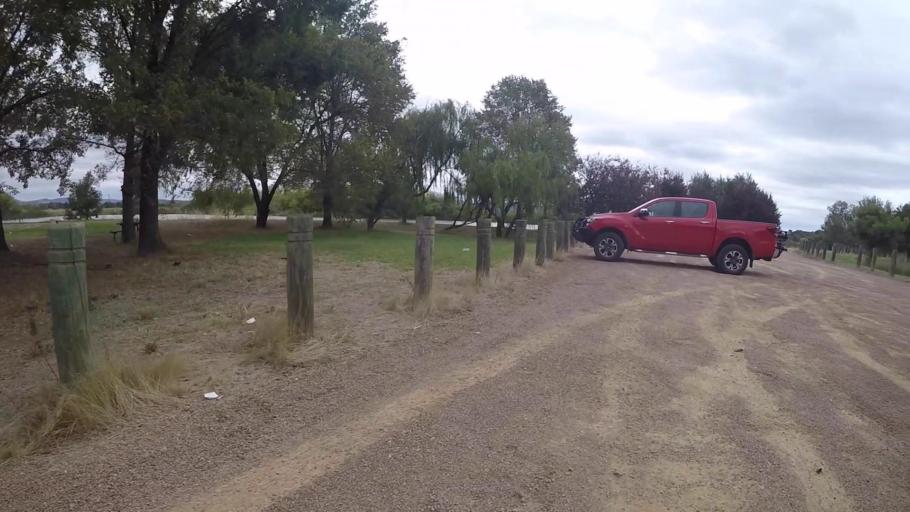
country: AU
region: Australian Capital Territory
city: Forrest
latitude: -35.3041
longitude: 149.1623
